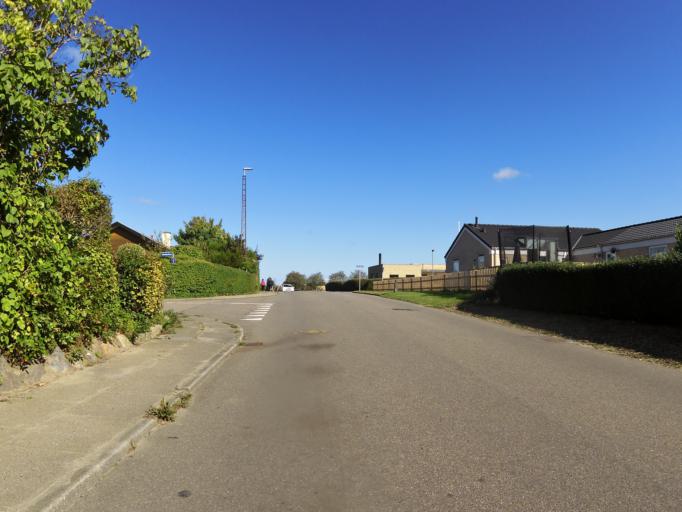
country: DK
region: South Denmark
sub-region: Sonderborg Kommune
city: Dybbol
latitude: 54.9465
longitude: 9.7031
